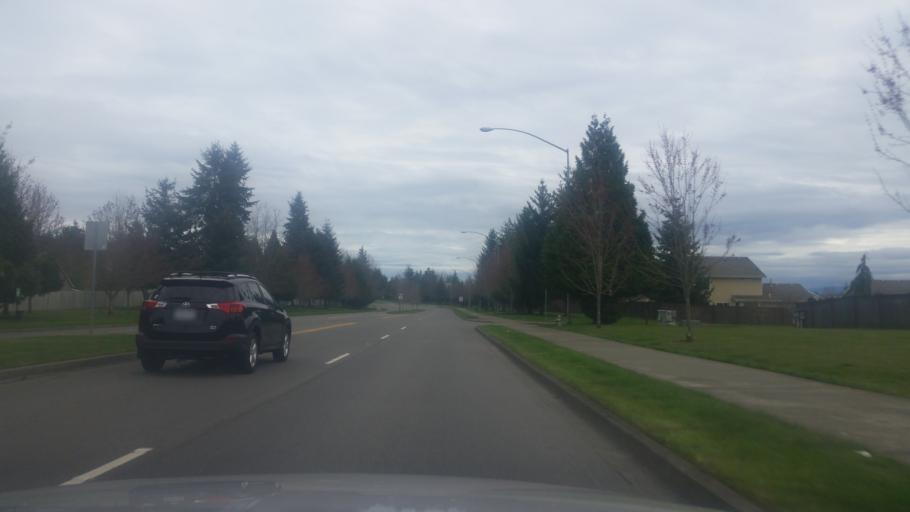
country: US
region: Washington
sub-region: Pierce County
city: McMillin
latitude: 47.1026
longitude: -122.2516
